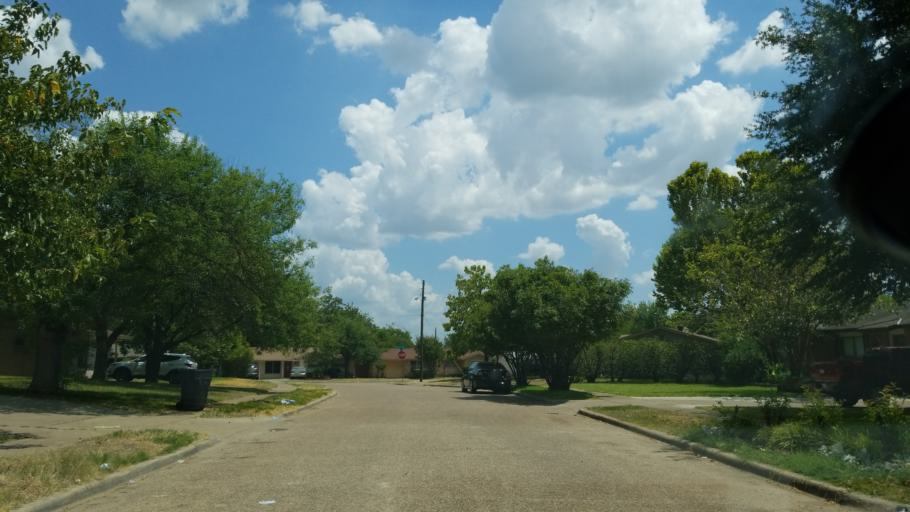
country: US
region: Texas
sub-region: Dallas County
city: Cockrell Hill
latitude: 32.7164
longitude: -96.8942
